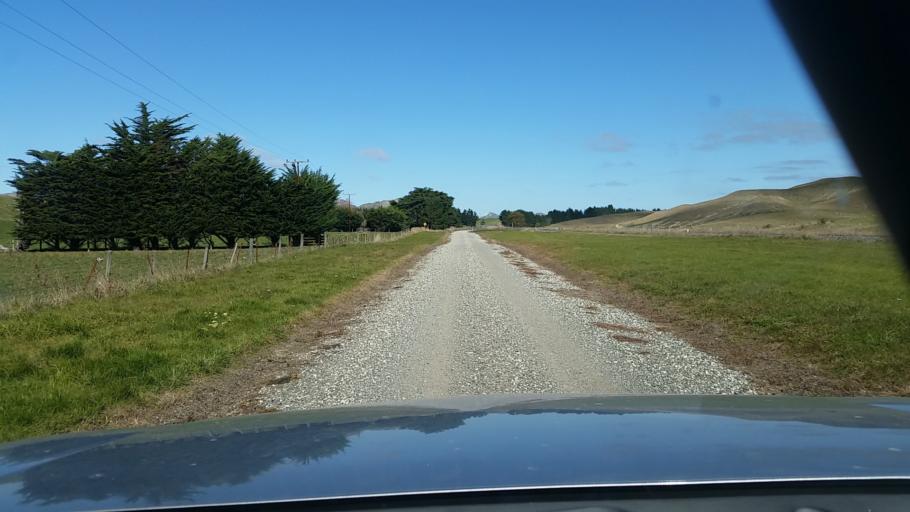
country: NZ
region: Marlborough
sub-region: Marlborough District
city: Blenheim
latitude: -41.7518
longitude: 174.1593
